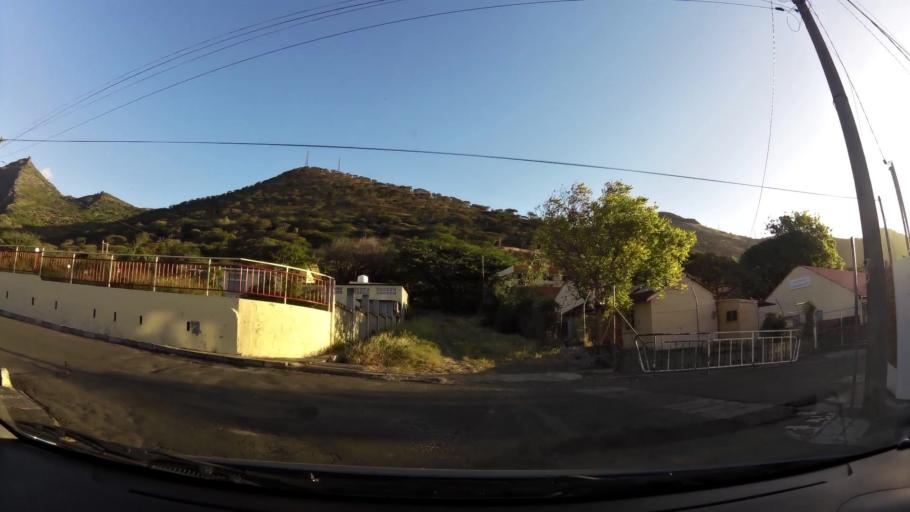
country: MU
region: Port Louis
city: Port Louis
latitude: -20.1755
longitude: 57.5067
